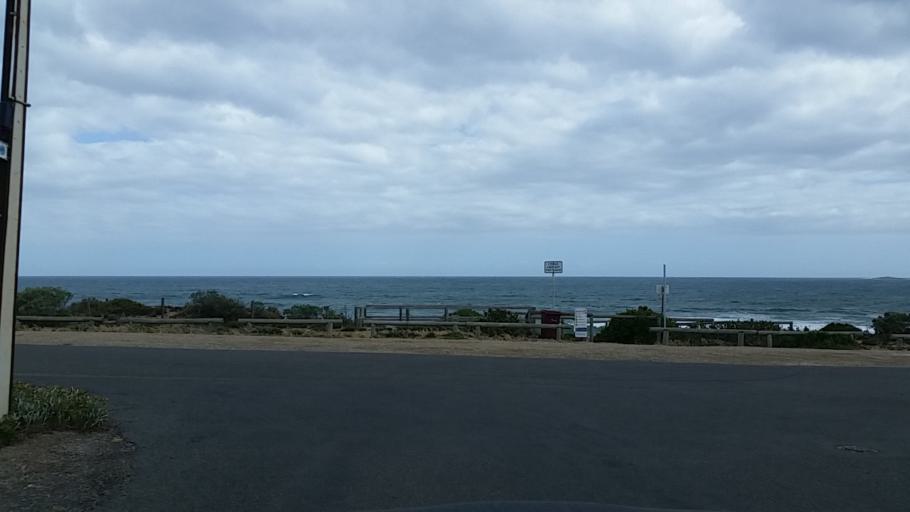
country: AU
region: South Australia
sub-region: Alexandrina
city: Port Elliot
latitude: -35.5353
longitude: 138.6695
